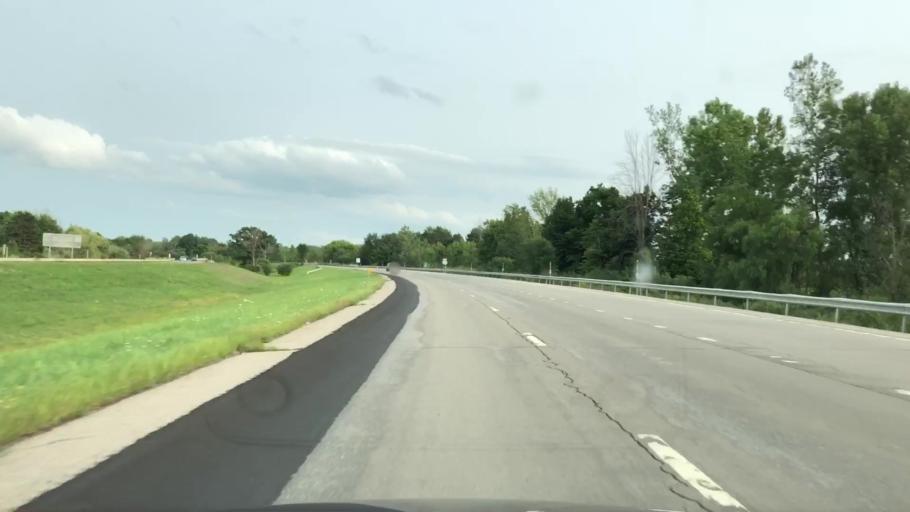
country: US
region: New York
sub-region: Erie County
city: Billington Heights
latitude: 42.8013
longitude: -78.6393
